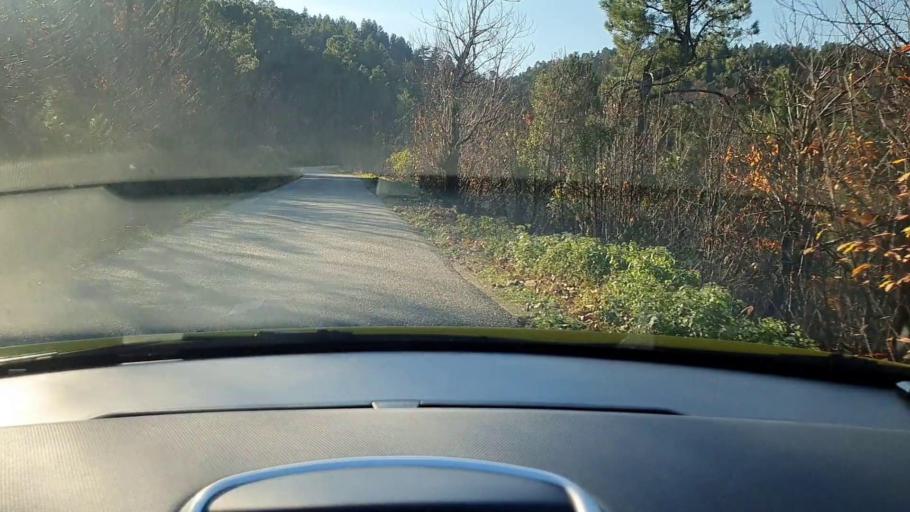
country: FR
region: Languedoc-Roussillon
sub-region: Departement du Gard
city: Branoux-les-Taillades
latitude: 44.2869
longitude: 3.9778
